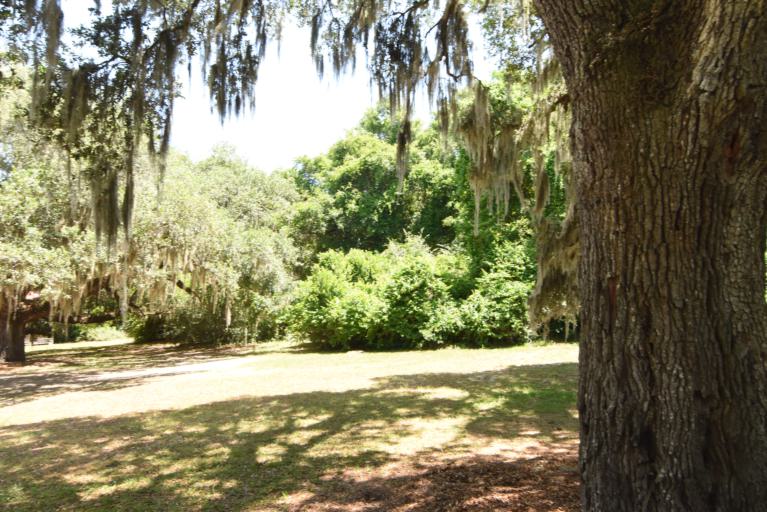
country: US
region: South Carolina
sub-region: Charleston County
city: Charleston
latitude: 32.7628
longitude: -79.9721
